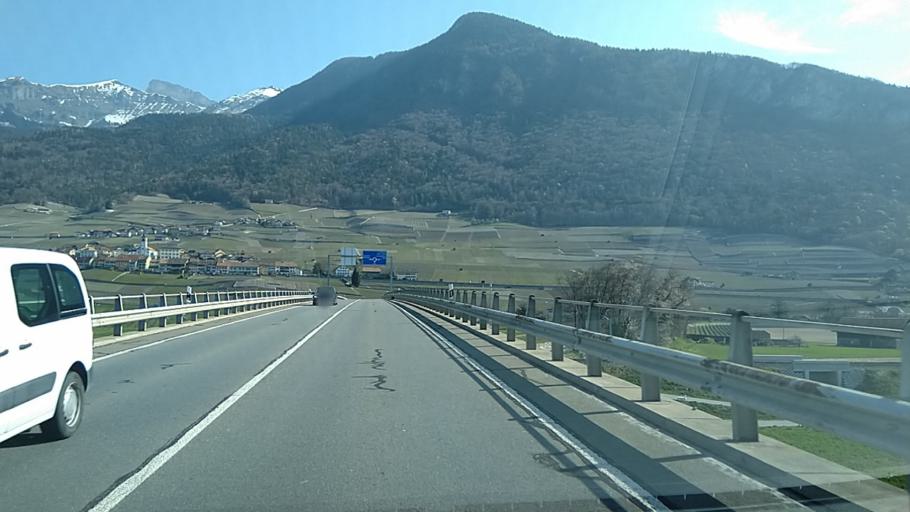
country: CH
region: Vaud
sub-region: Aigle District
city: Aigle
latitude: 46.3247
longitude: 6.9548
